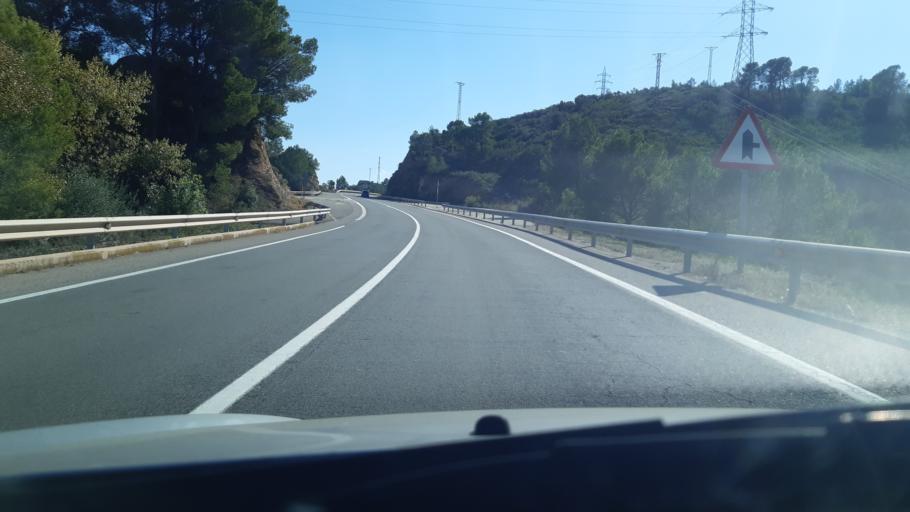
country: ES
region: Catalonia
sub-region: Provincia de Tarragona
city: Tivenys
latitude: 40.9299
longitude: 0.4849
